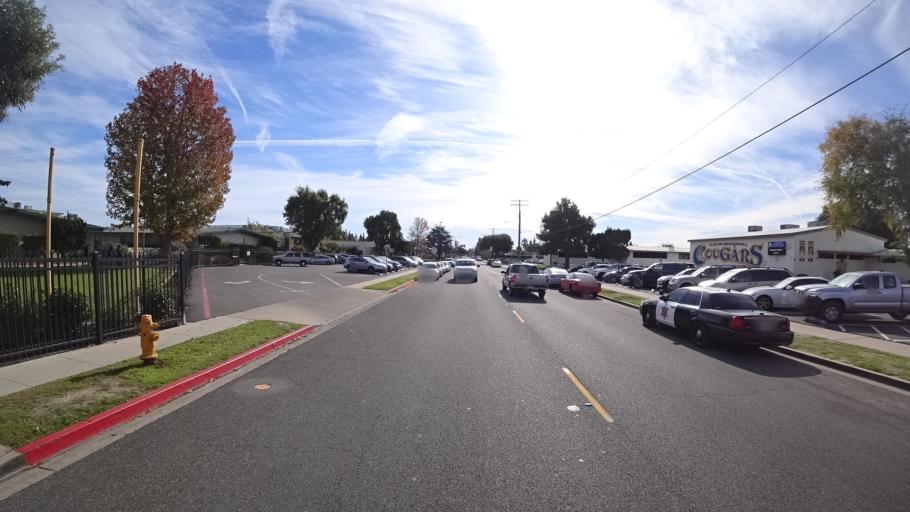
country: US
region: California
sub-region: Orange County
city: Garden Grove
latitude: 33.7650
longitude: -117.9116
